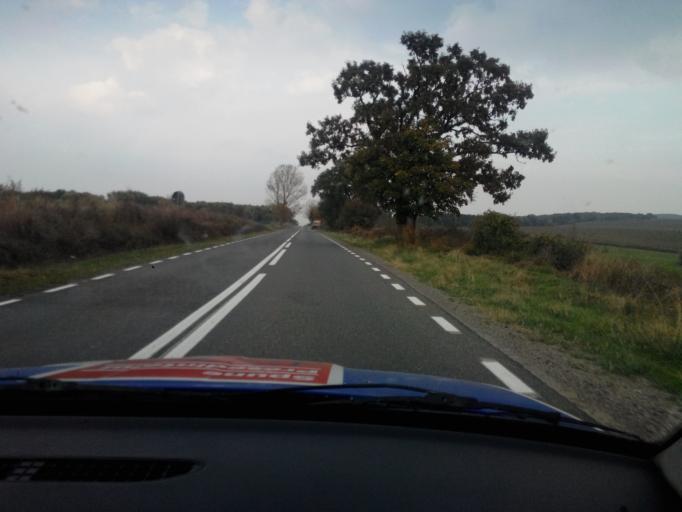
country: RO
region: Tulcea
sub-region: Comuna Somova
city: Somova
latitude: 45.1771
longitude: 28.6054
